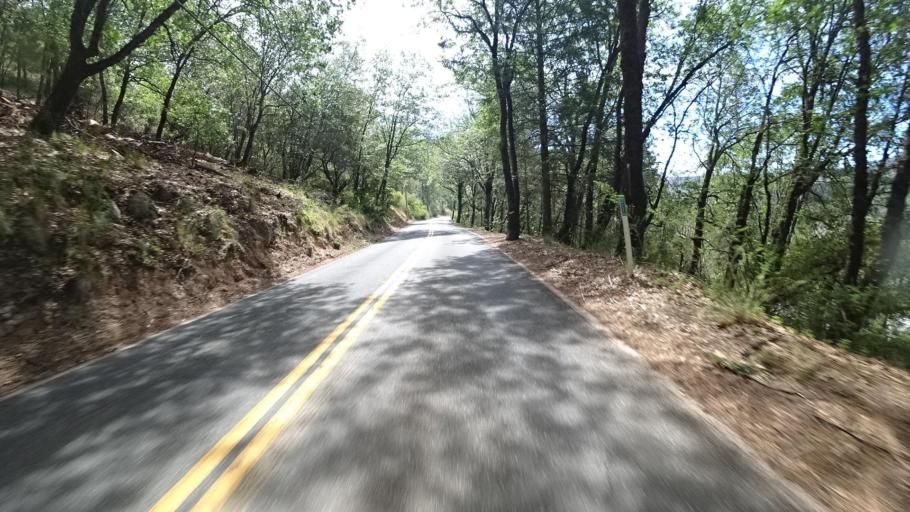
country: US
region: California
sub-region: Lake County
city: Cobb
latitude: 38.8604
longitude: -122.7089
